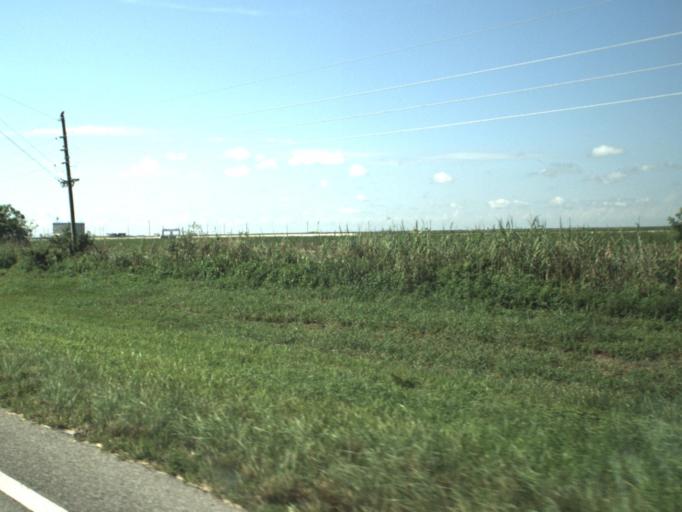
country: US
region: Florida
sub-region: Palm Beach County
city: Belle Glade Camp
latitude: 26.4060
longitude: -80.5930
